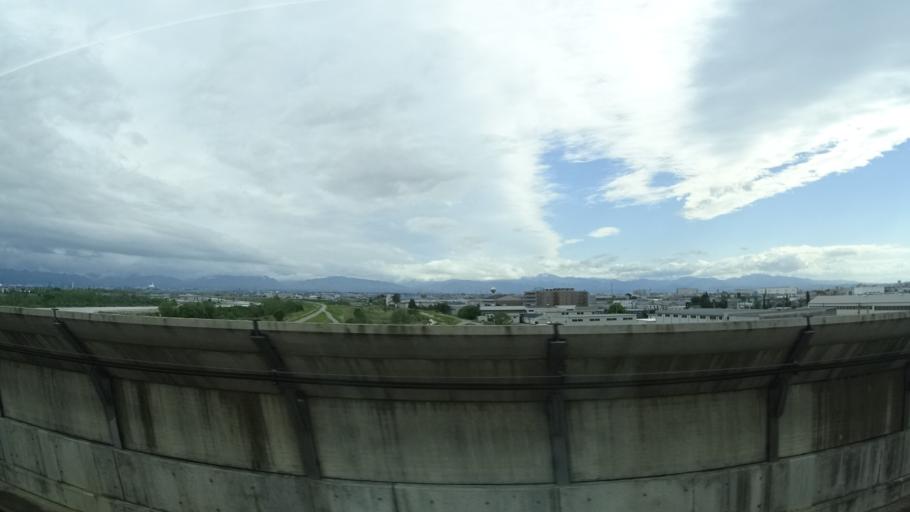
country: JP
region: Toyama
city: Toyama-shi
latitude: 36.7150
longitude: 137.2705
